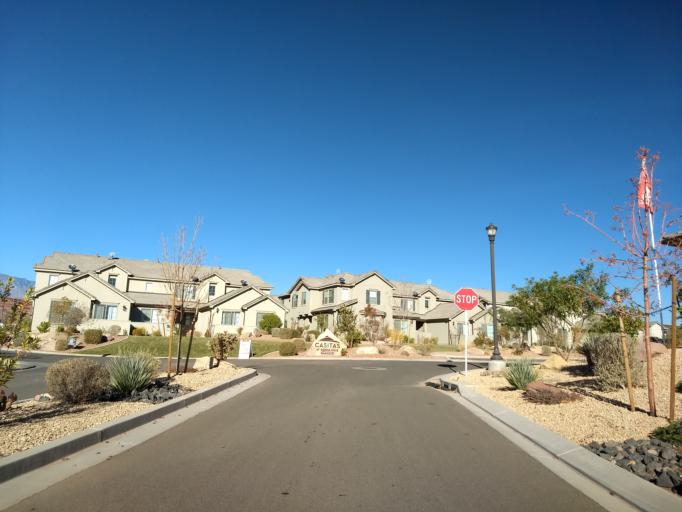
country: US
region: Utah
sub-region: Washington County
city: Washington
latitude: 37.1444
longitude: -113.4787
